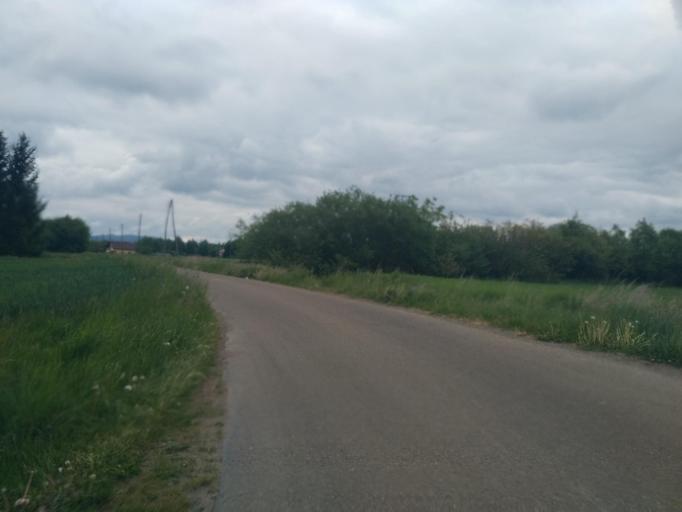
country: PL
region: Subcarpathian Voivodeship
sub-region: Powiat krosnienski
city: Jedlicze
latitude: 49.7086
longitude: 21.6808
